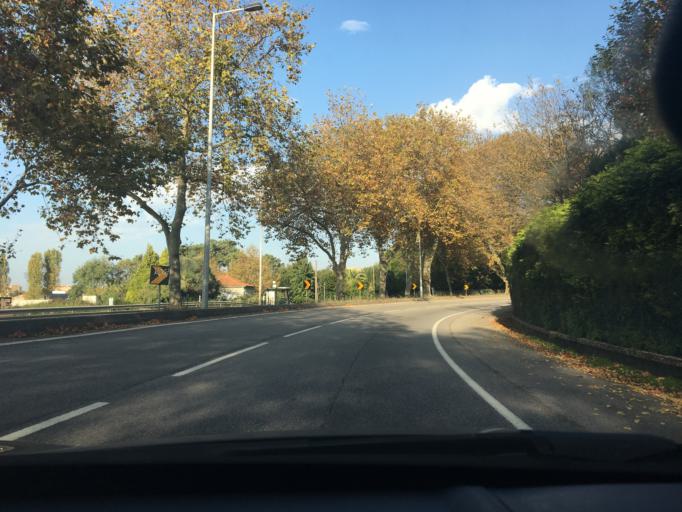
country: PT
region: Porto
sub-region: Matosinhos
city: Senhora da Hora
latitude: 41.1787
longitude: -8.6670
